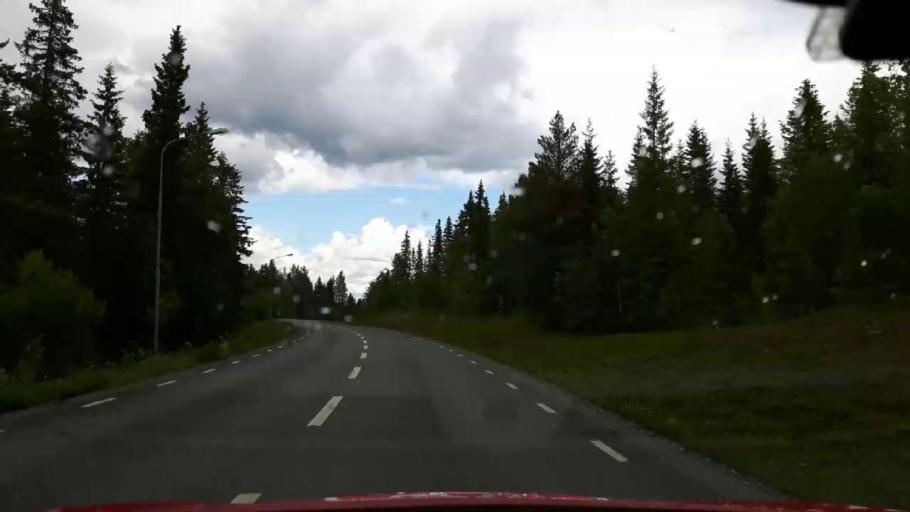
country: SE
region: Jaemtland
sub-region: Krokoms Kommun
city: Krokom
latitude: 63.7595
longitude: 14.3119
